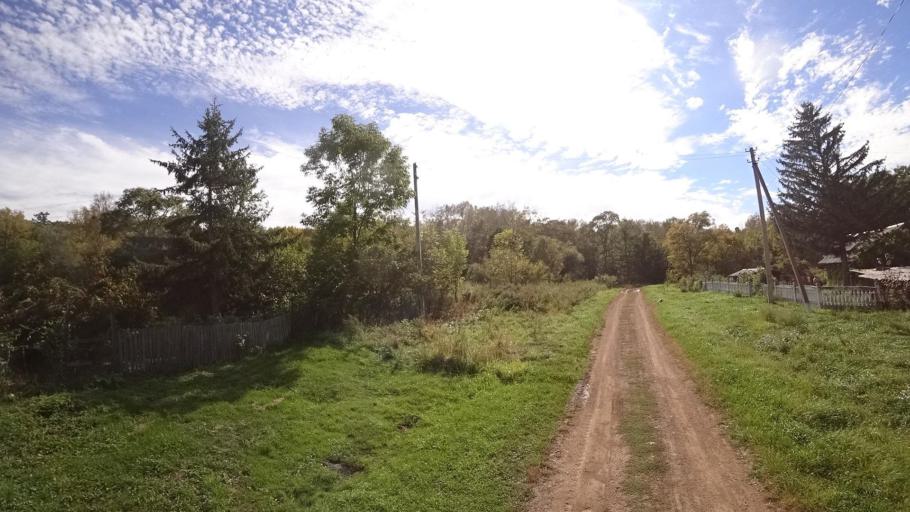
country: RU
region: Primorskiy
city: Yakovlevka
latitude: 44.3863
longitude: 133.5986
